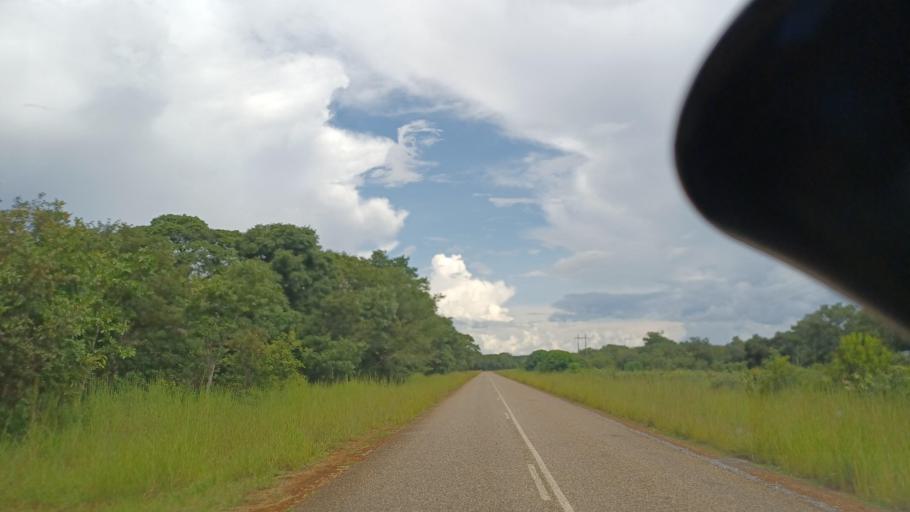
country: ZM
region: North-Western
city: Kasempa
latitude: -13.1560
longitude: 25.8790
